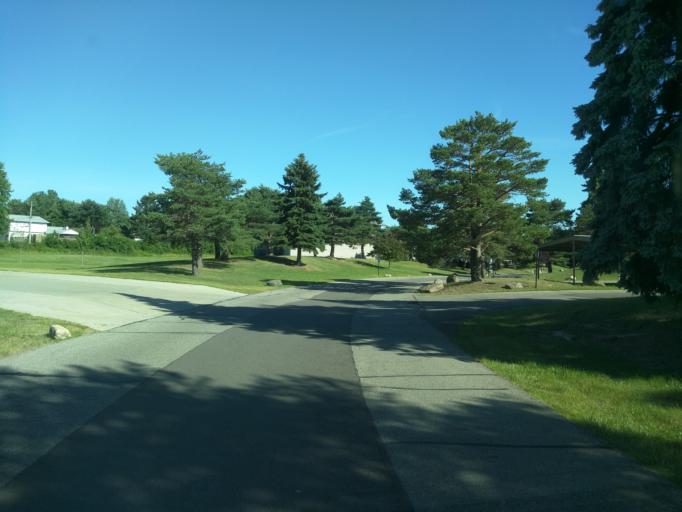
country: US
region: Michigan
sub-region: Eaton County
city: Waverly
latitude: 42.7394
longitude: -84.6388
